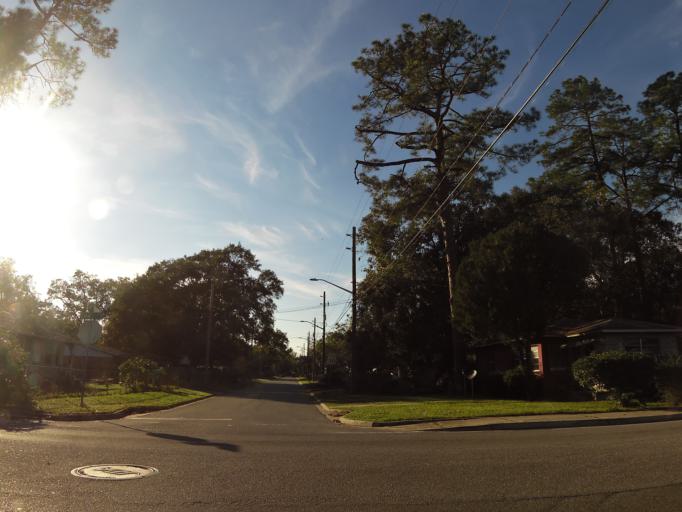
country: US
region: Florida
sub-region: Duval County
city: Jacksonville
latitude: 30.3546
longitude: -81.6971
